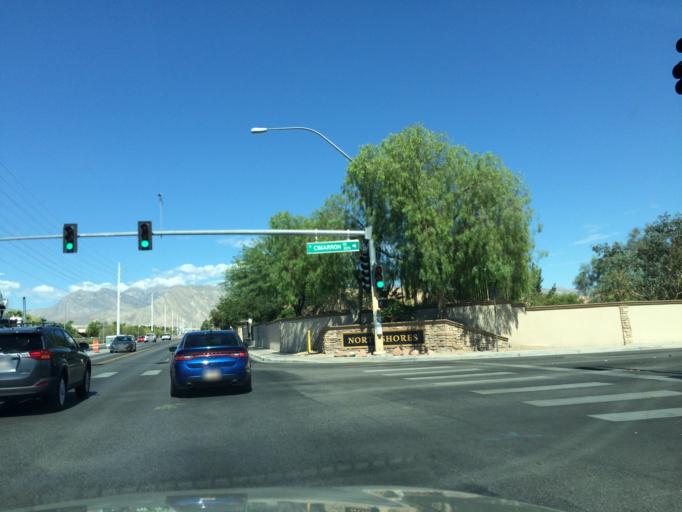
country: US
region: Nevada
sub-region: Clark County
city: Spring Valley
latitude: 36.2185
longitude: -115.2649
